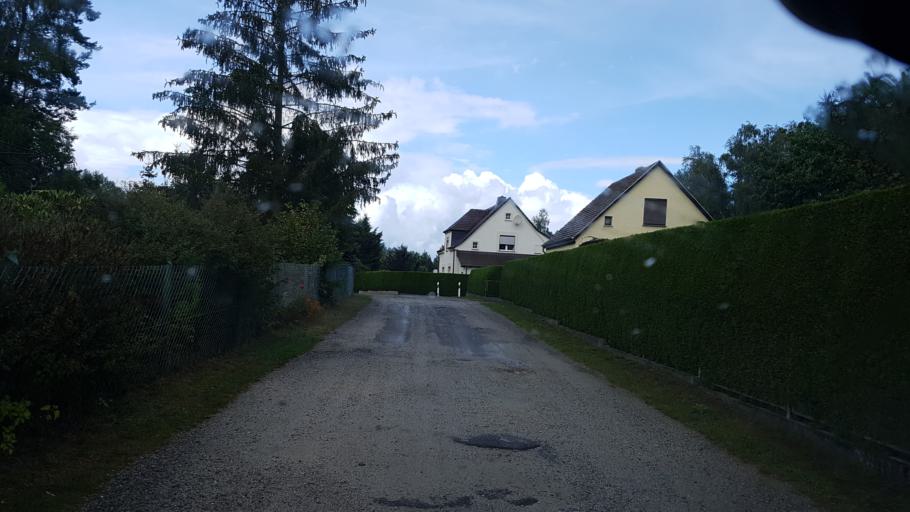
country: DE
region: Brandenburg
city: Tschernitz
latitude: 51.6054
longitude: 14.5949
